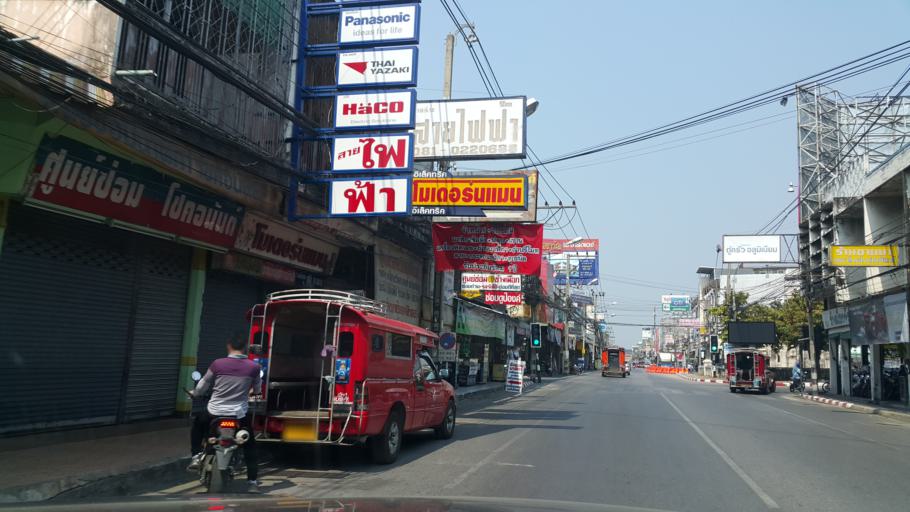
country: TH
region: Chiang Mai
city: Chiang Mai
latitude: 18.7999
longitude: 98.9860
